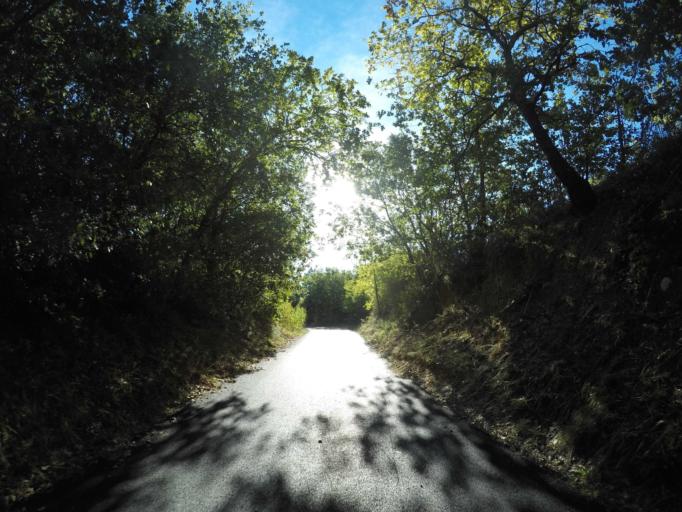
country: FR
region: Languedoc-Roussillon
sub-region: Departement des Pyrenees-Orientales
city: Trouillas
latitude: 42.5754
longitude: 2.7866
